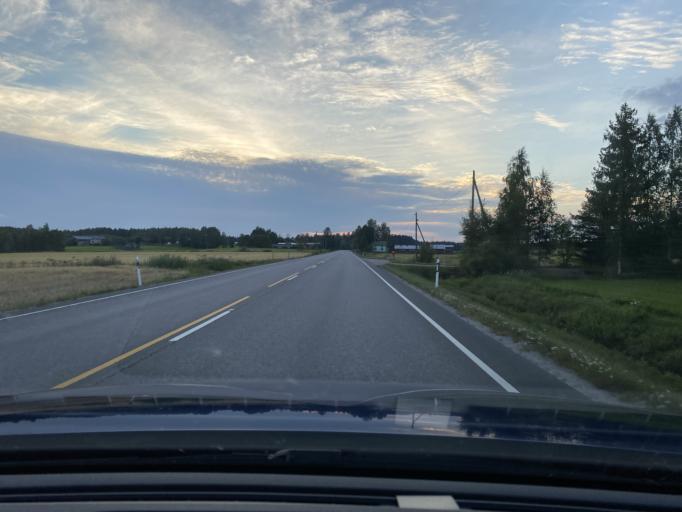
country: FI
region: Satakunta
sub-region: Pohjois-Satakunta
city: Kankaanpaeae
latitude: 61.7625
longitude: 22.4966
